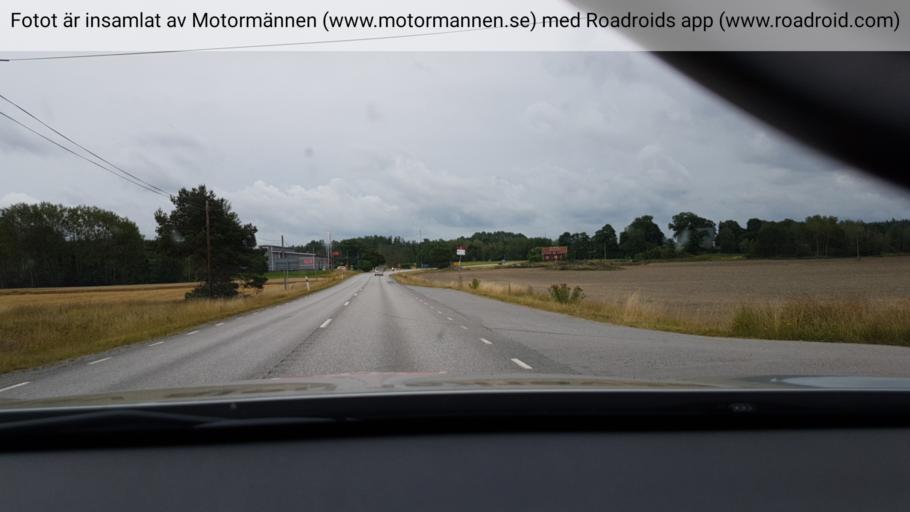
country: SE
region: Stockholm
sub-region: Vallentuna Kommun
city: Vallentuna
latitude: 59.6712
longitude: 18.0466
